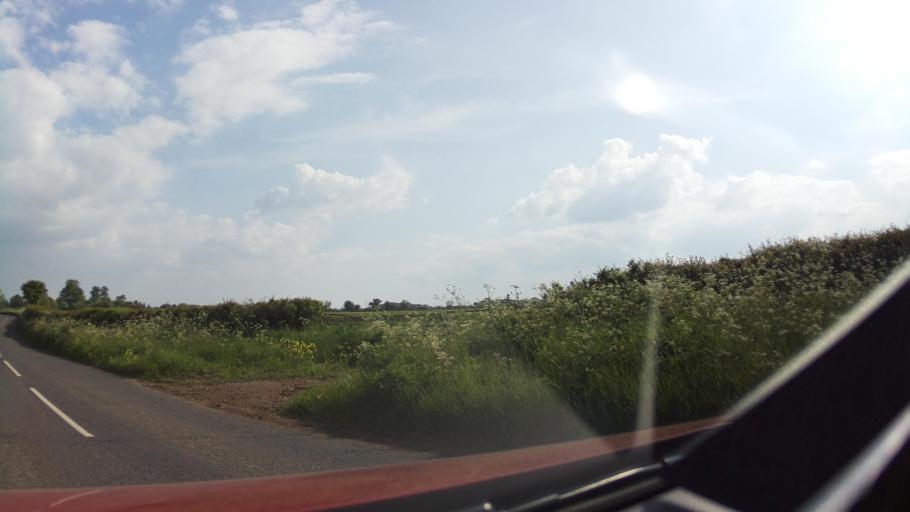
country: GB
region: England
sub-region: Wiltshire
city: Norton
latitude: 51.5513
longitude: -2.1532
